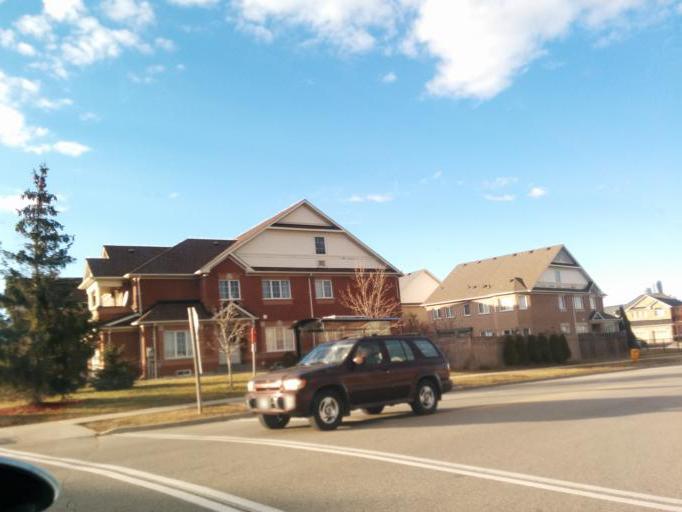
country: CA
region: Ontario
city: Mississauga
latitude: 43.5726
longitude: -79.6315
